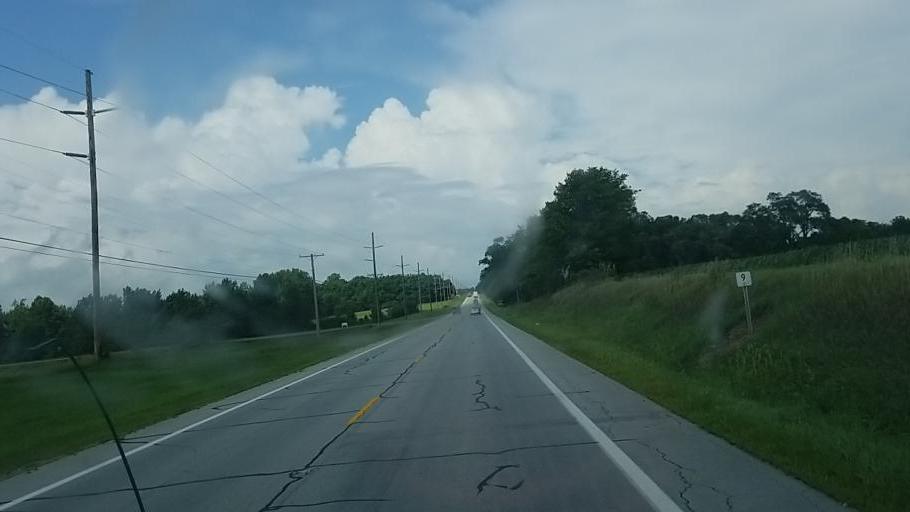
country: US
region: Ohio
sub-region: Champaign County
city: Urbana
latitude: 40.1419
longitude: -83.7468
